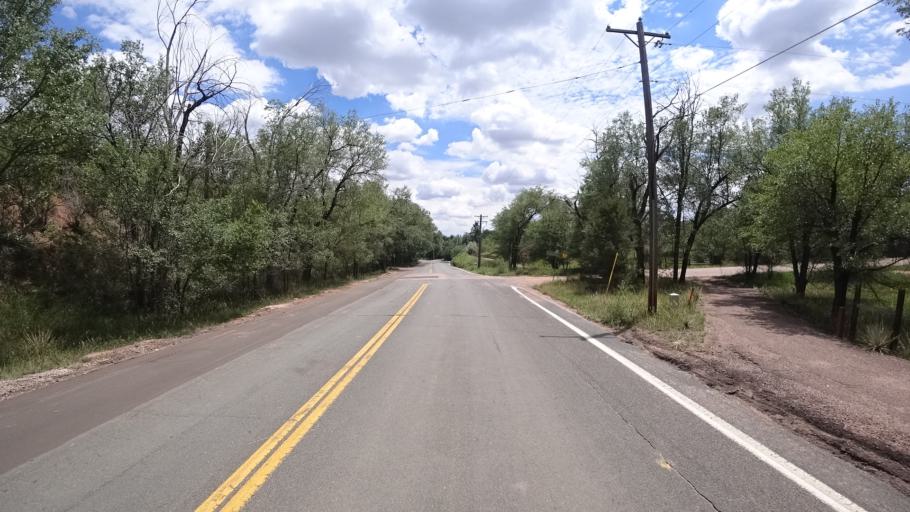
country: US
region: Colorado
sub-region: El Paso County
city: Colorado Springs
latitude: 38.8521
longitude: -104.8418
